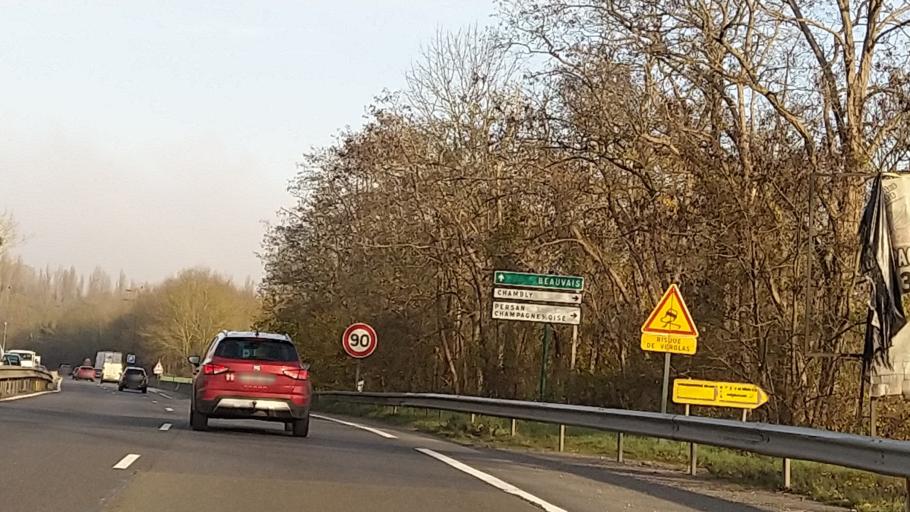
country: FR
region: Ile-de-France
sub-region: Departement du Val-d'Oise
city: Mours
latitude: 49.1298
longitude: 2.2560
